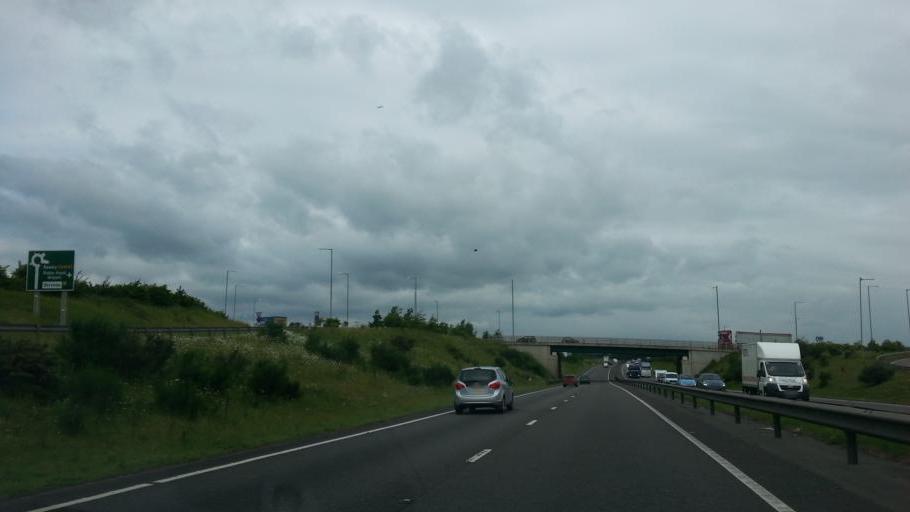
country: GB
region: England
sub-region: Nottinghamshire
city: Bircotes
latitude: 53.3870
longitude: -1.0619
